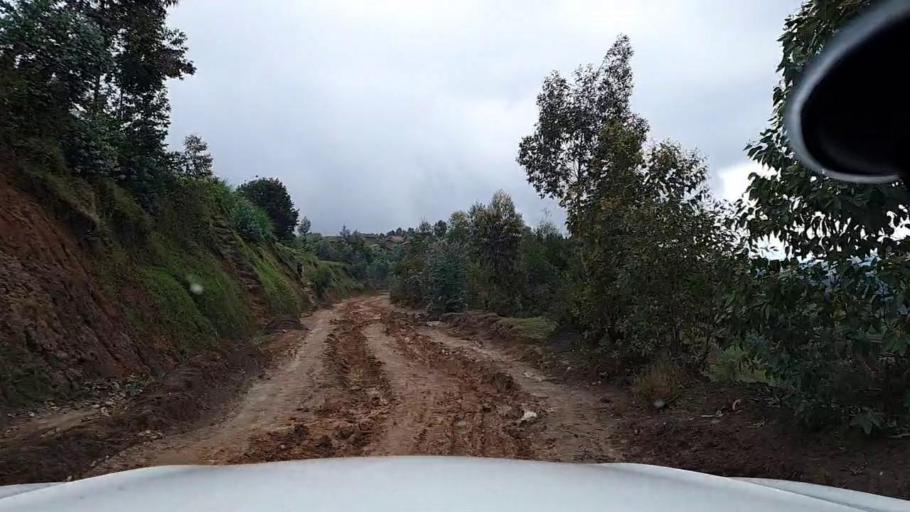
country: RW
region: Western Province
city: Kibuye
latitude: -2.0834
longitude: 29.5110
